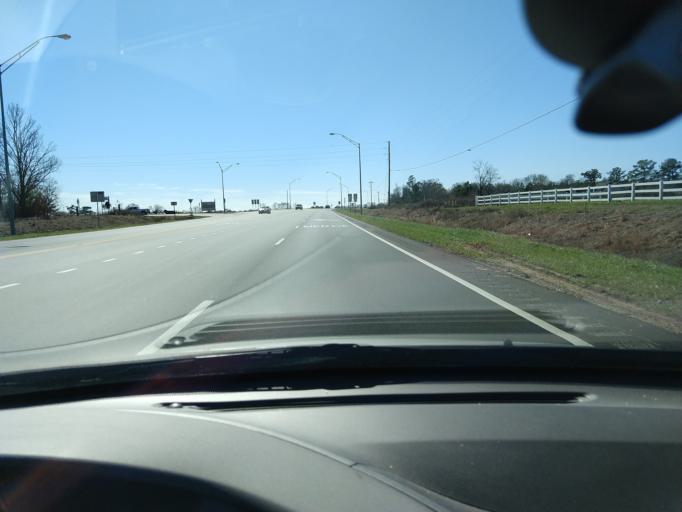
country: US
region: Alabama
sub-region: Covington County
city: Andalusia
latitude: 31.2790
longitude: -86.5060
